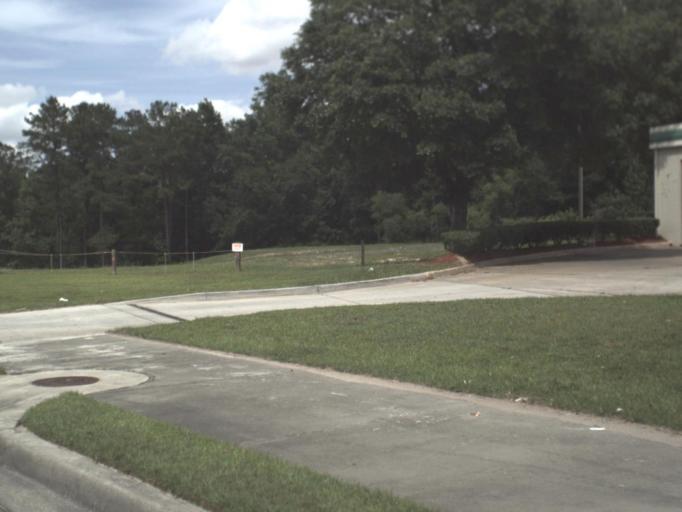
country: US
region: Florida
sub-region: Clay County
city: Middleburg
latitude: 30.0742
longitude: -81.8641
